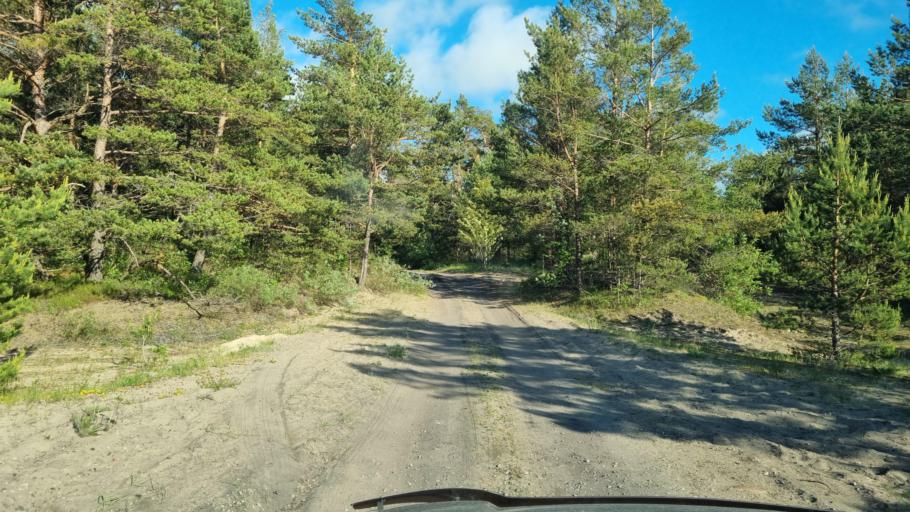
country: LV
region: Ventspils
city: Ventspils
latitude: 57.3642
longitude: 21.5094
